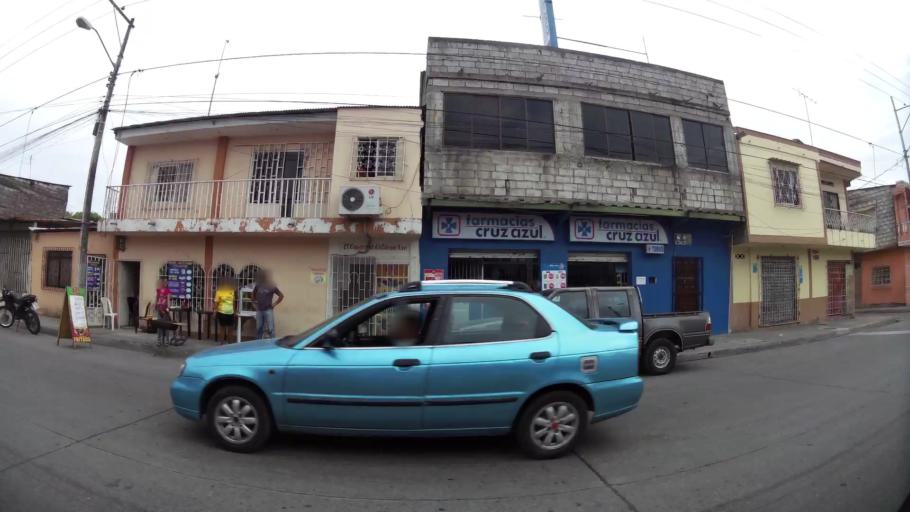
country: EC
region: Guayas
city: Guayaquil
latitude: -2.2529
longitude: -79.8761
